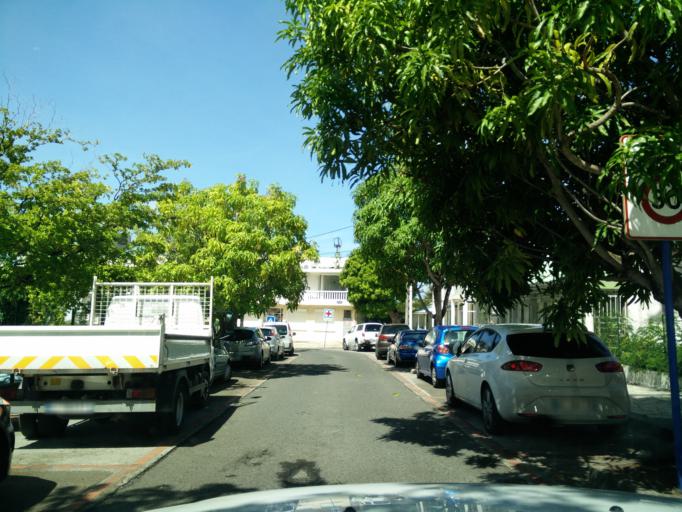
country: GP
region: Guadeloupe
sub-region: Guadeloupe
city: Basse-Terre
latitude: 15.9951
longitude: -61.7259
